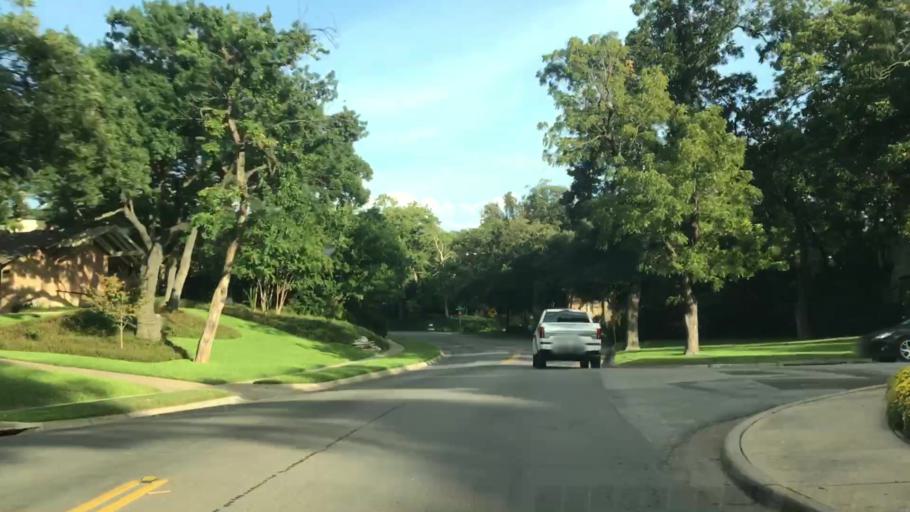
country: US
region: Texas
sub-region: Dallas County
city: Cockrell Hill
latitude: 32.7590
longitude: -96.8474
